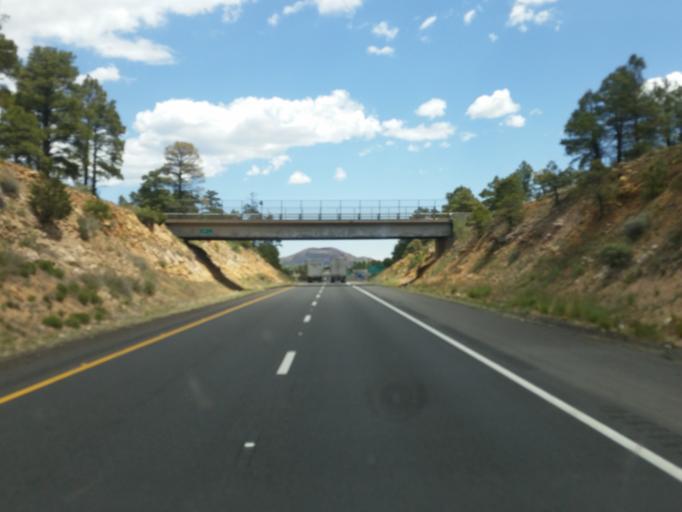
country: US
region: Arizona
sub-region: Coconino County
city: Flagstaff
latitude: 35.2012
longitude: -111.6086
